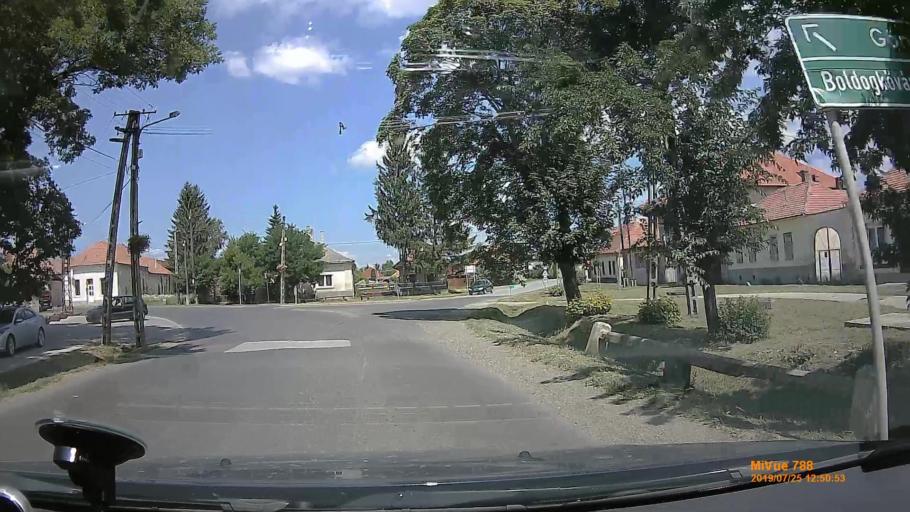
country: HU
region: Borsod-Abauj-Zemplen
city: Abaujszanto
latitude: 48.2831
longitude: 21.1874
